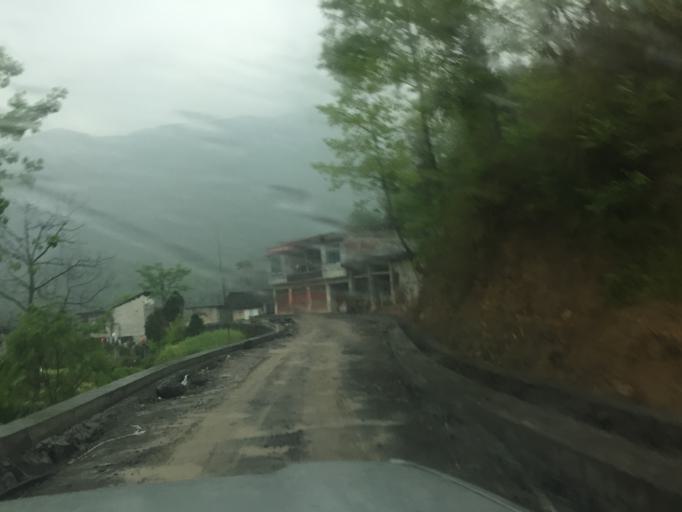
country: CN
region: Guizhou Sheng
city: Changfeng
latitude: 28.4281
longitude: 108.0816
